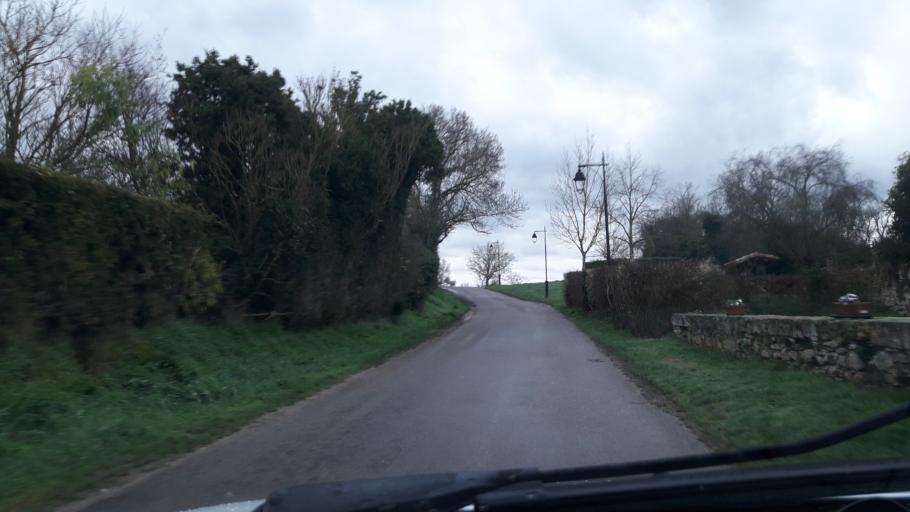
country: FR
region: Midi-Pyrenees
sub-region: Departement du Gers
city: Gimont
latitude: 43.6899
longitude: 0.9168
